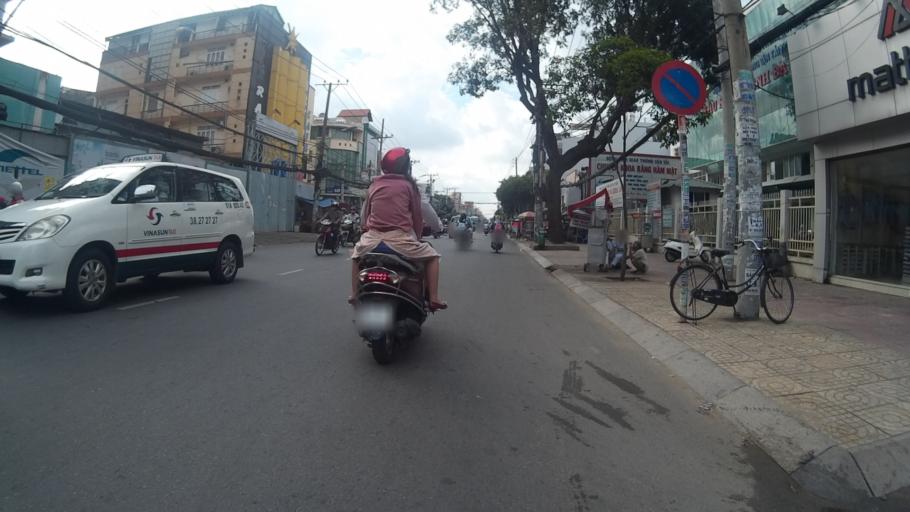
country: VN
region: Ho Chi Minh City
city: Quan Ba
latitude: 10.7785
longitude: 106.6804
